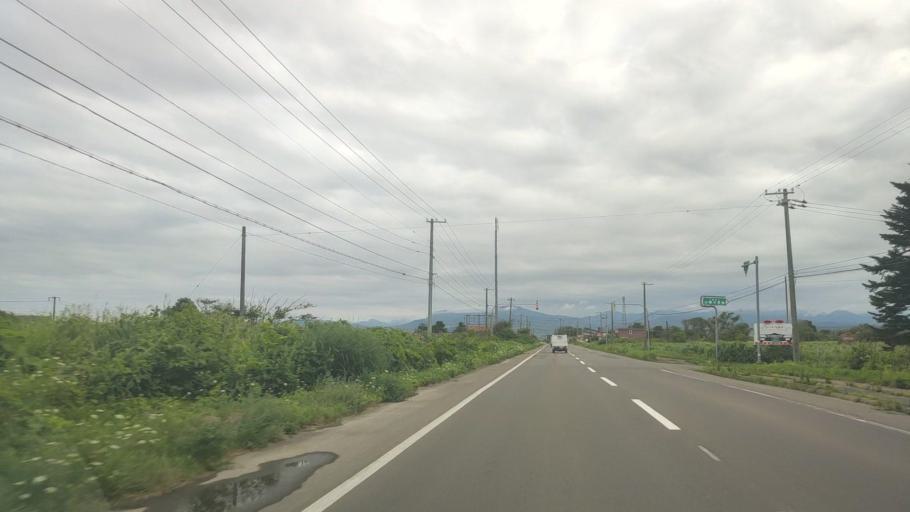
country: JP
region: Hokkaido
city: Nanae
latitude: 42.3178
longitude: 140.2747
